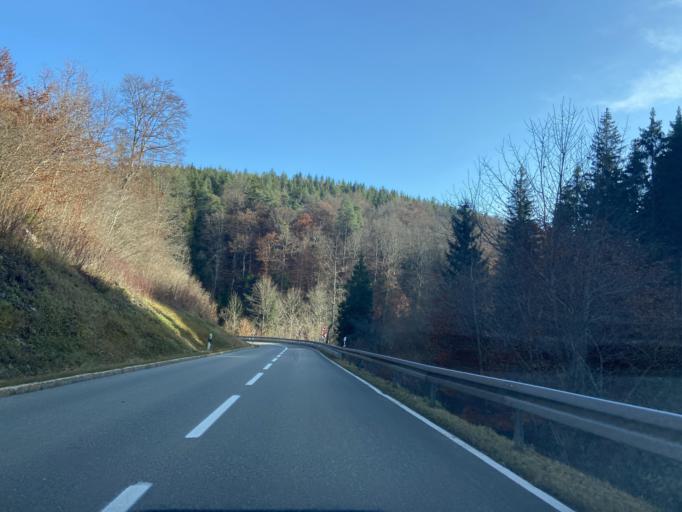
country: DE
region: Baden-Wuerttemberg
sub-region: Tuebingen Region
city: Stetten am Kalten Markt
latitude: 48.1056
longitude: 9.0923
